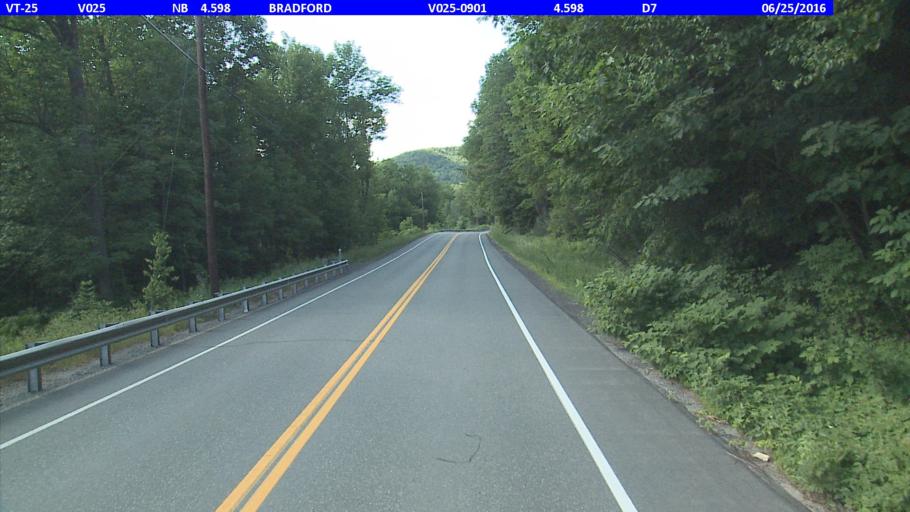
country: US
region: New Hampshire
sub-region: Grafton County
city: Haverhill
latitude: 44.0189
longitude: -72.1731
